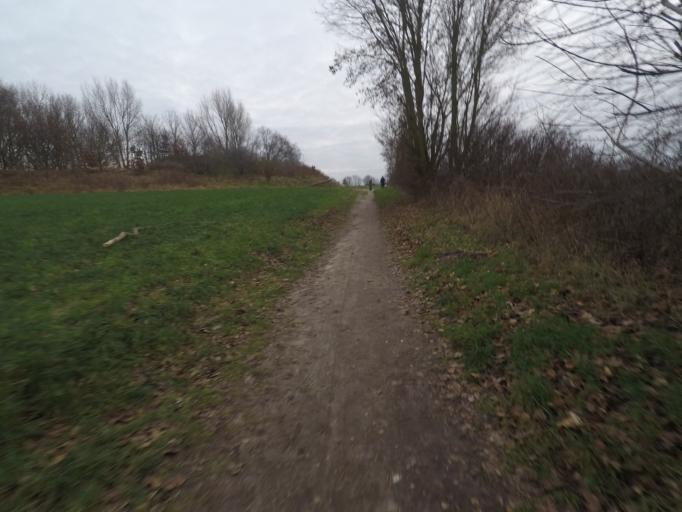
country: DE
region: Lower Saxony
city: Langen
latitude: 53.6039
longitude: 8.6001
